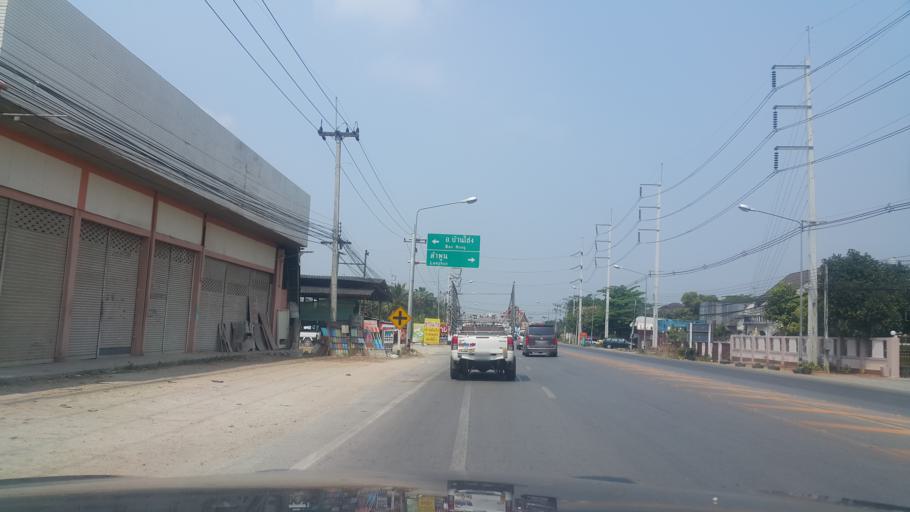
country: TH
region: Lamphun
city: Pa Sang
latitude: 18.4850
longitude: 98.9403
